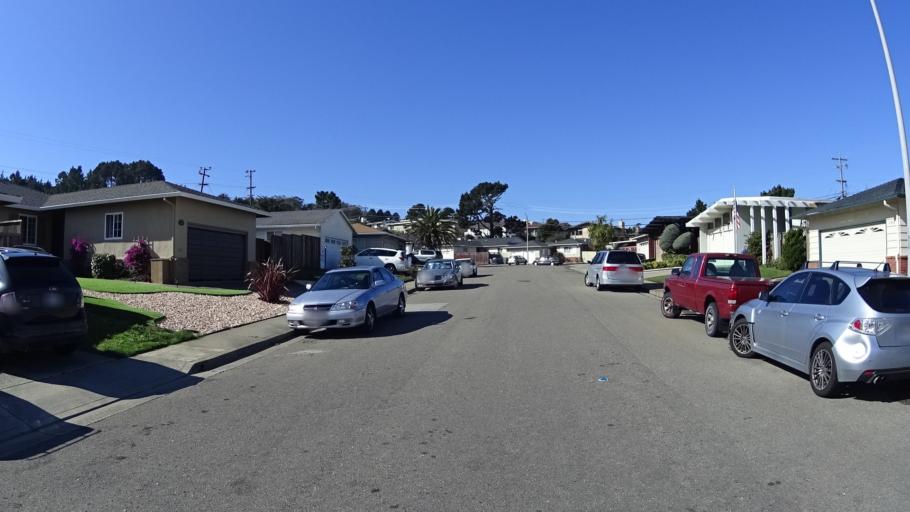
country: US
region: California
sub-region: San Mateo County
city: Colma
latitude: 37.6398
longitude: -122.4583
